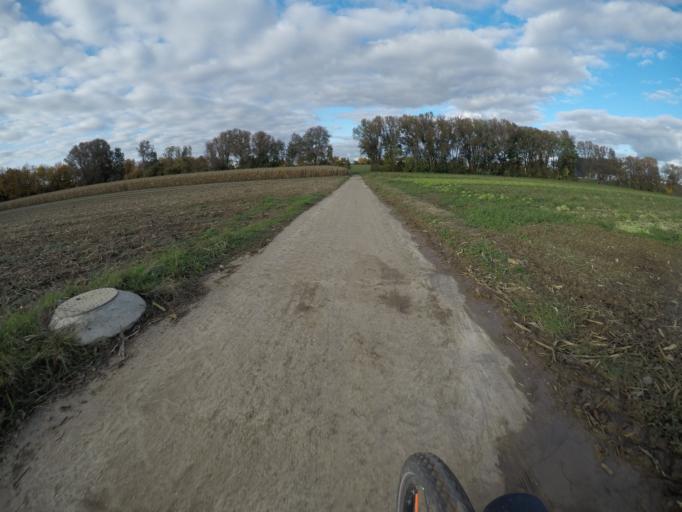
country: DE
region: Baden-Wuerttemberg
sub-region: Regierungsbezirk Stuttgart
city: Leinfelden-Echterdingen
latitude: 48.6748
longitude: 9.1902
